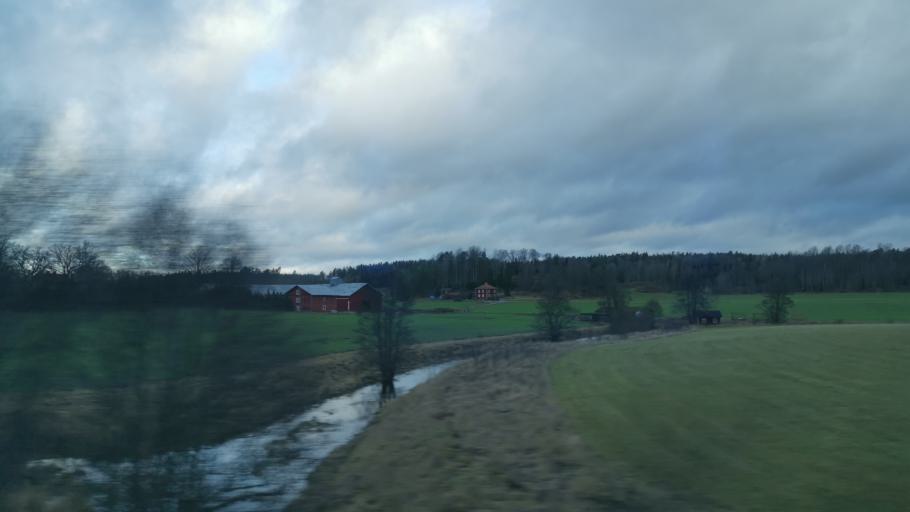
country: SE
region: Stockholm
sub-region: Sodertalje Kommun
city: Molnbo
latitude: 59.0439
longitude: 17.4017
